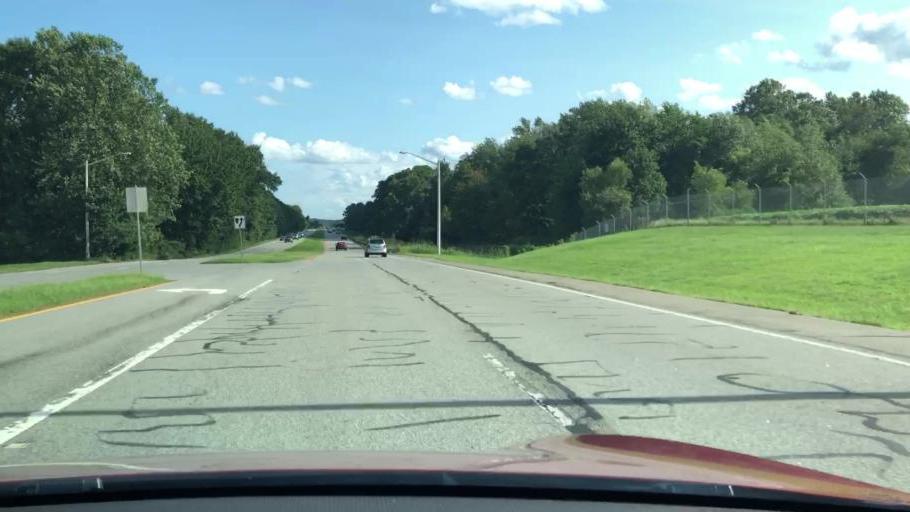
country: US
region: Virginia
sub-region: City of Virginia Beach
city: Virginia Beach
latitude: 36.8361
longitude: -76.0129
